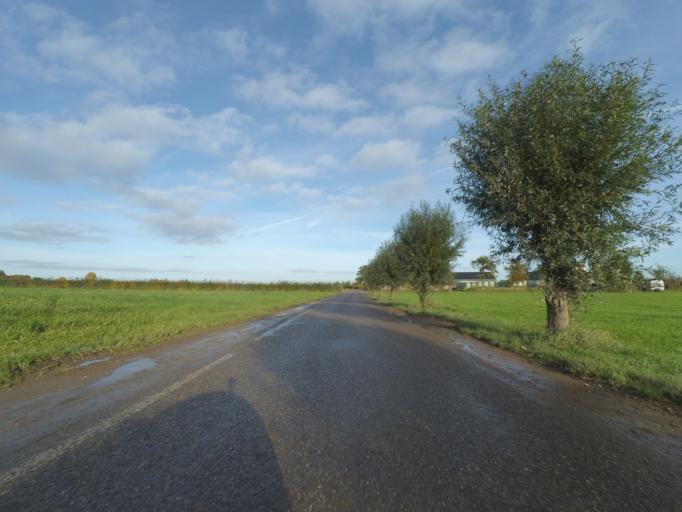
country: NL
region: Utrecht
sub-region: Gemeente Utrechtse Heuvelrug
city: Driebergen-Rijsenburg
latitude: 52.0001
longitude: 5.2653
